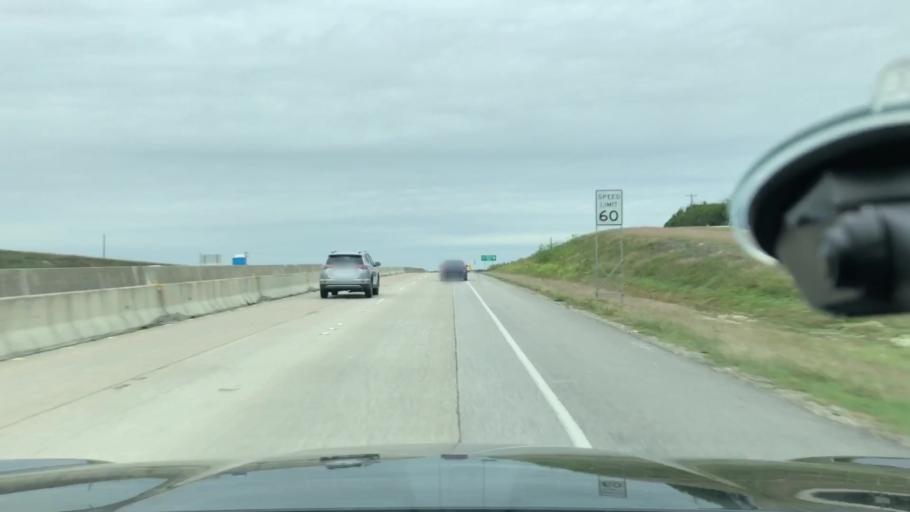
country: US
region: Texas
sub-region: Ellis County
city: Waxahachie
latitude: 32.3829
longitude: -96.8667
